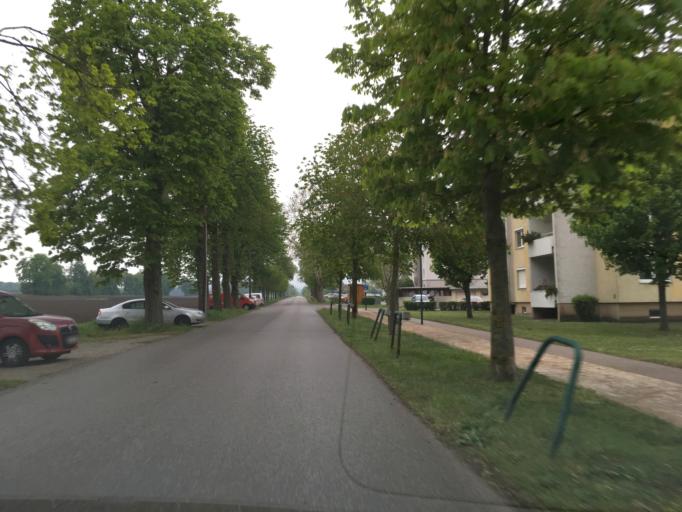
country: AT
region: Lower Austria
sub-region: Politischer Bezirk Bruck an der Leitha
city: Bruck an der Leitha
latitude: 48.0150
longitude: 16.7731
